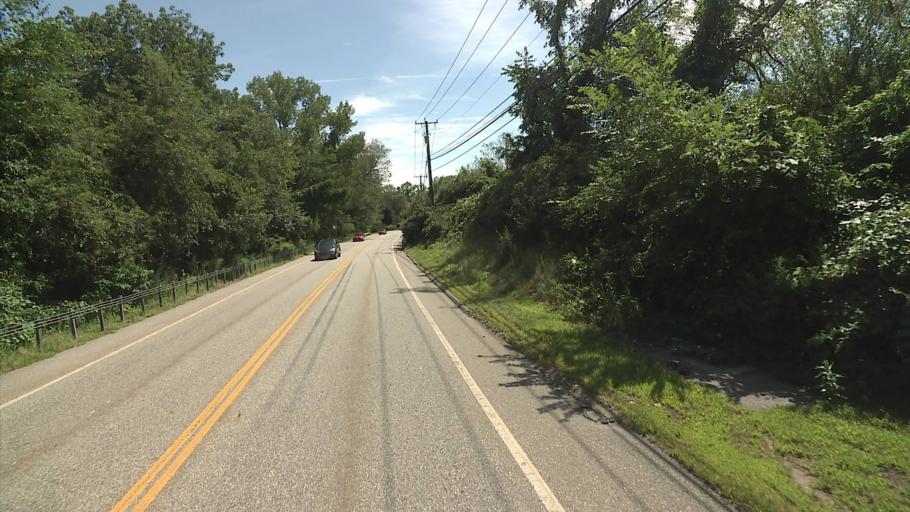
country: US
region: Connecticut
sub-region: Windham County
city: East Brooklyn
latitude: 41.8508
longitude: -71.9398
